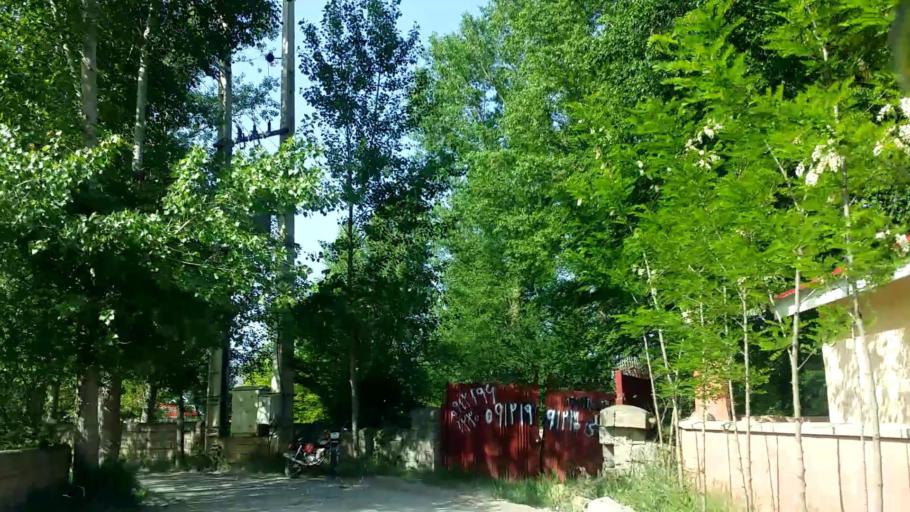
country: IR
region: Mazandaran
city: `Abbasabad
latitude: 36.5192
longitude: 51.1741
